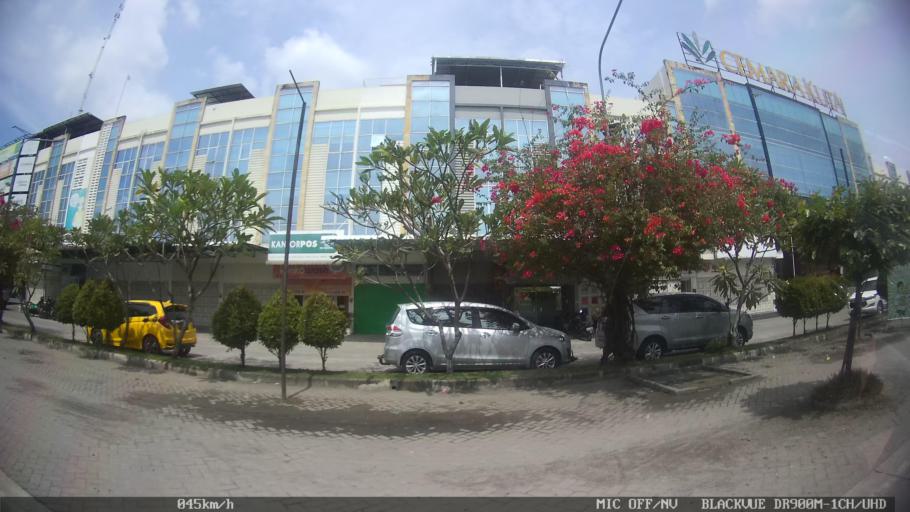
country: ID
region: North Sumatra
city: Medan
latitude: 3.6412
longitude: 98.7083
